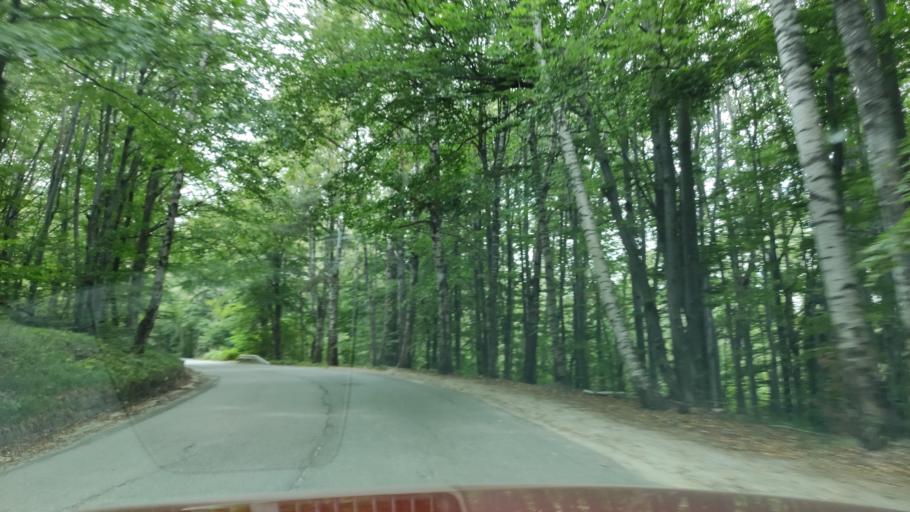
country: BG
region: Sofia-Capital
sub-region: Stolichna Obshtina
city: Sofia
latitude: 42.6225
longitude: 23.2284
